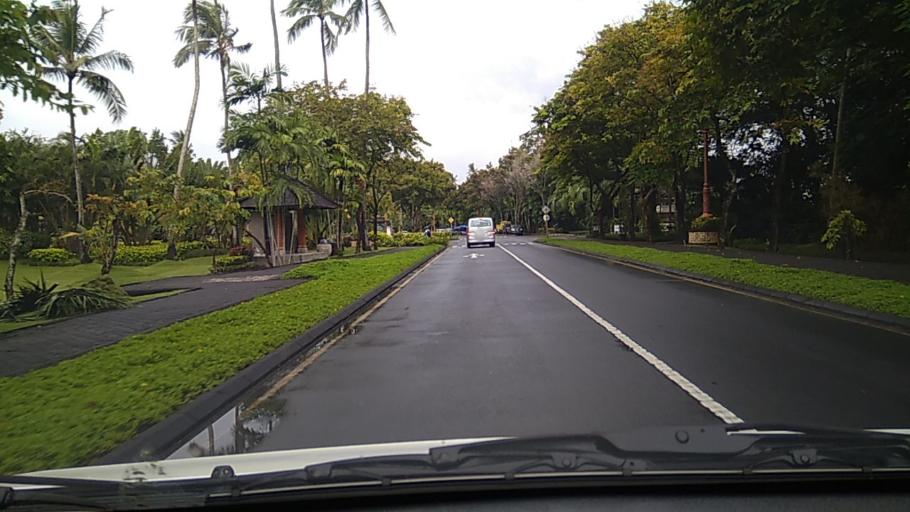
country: ID
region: Bali
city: Bualu
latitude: -8.7945
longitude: 115.2273
